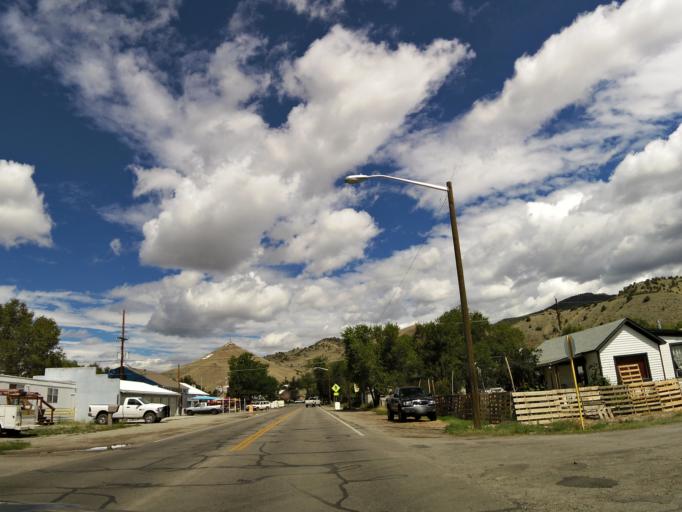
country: US
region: Colorado
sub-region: Chaffee County
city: Salida
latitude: 38.5300
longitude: -105.9847
